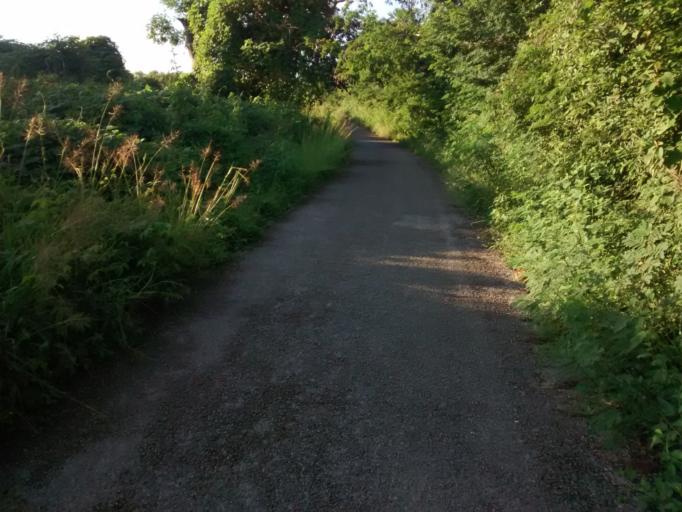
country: MX
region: Yucatan
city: Valladolid
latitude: 20.7170
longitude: -88.2226
